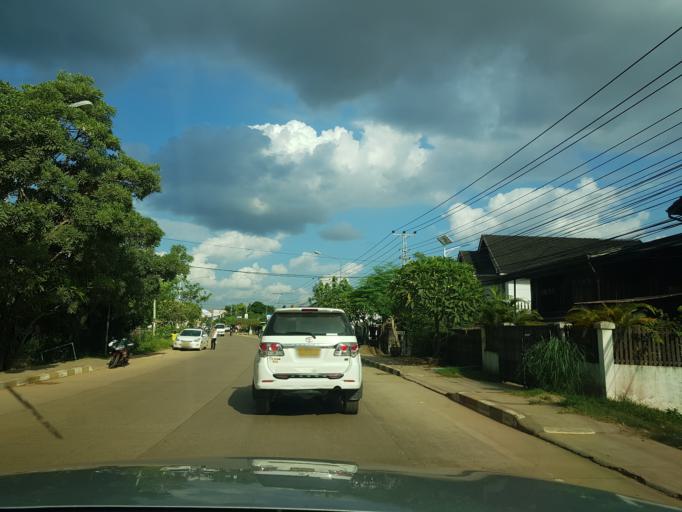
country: TH
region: Nong Khai
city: Si Chiang Mai
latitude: 17.9738
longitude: 102.5543
